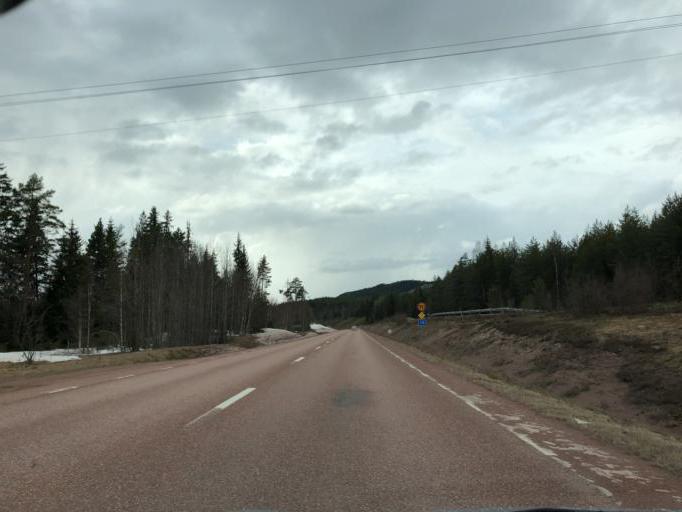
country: SE
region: Dalarna
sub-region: Alvdalens Kommun
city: AElvdalen
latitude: 61.2771
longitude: 13.9626
